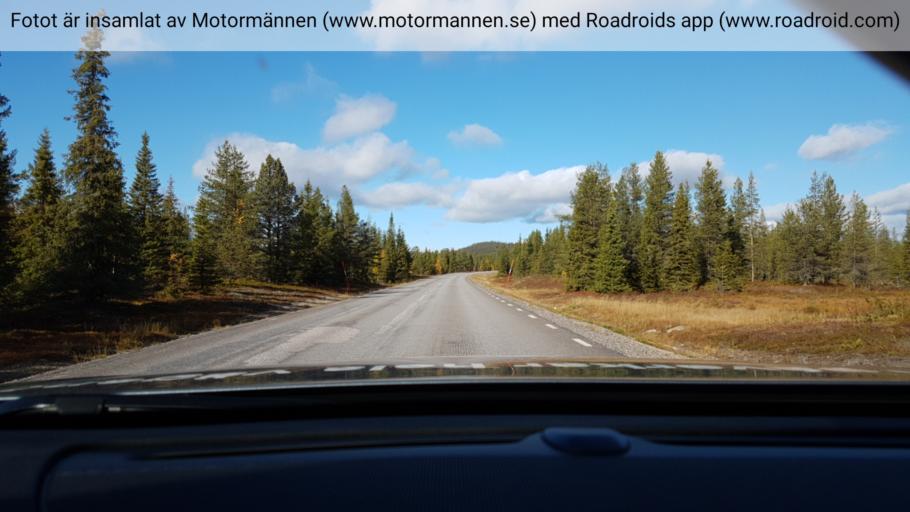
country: SE
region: Norrbotten
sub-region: Arjeplogs Kommun
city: Arjeplog
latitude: 65.8903
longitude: 18.3756
